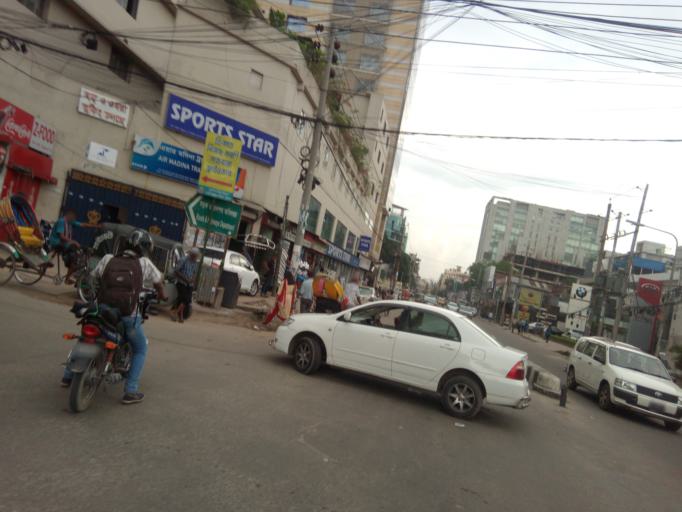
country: BD
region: Dhaka
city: Paltan
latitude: 23.7706
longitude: 90.4060
